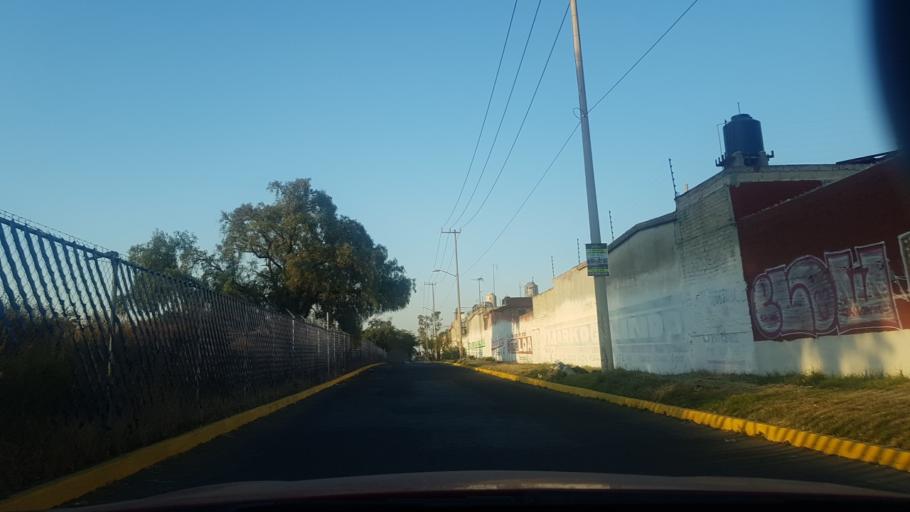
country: MX
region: Mexico
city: Cuautitlan Izcalli
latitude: 19.6407
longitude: -99.2216
